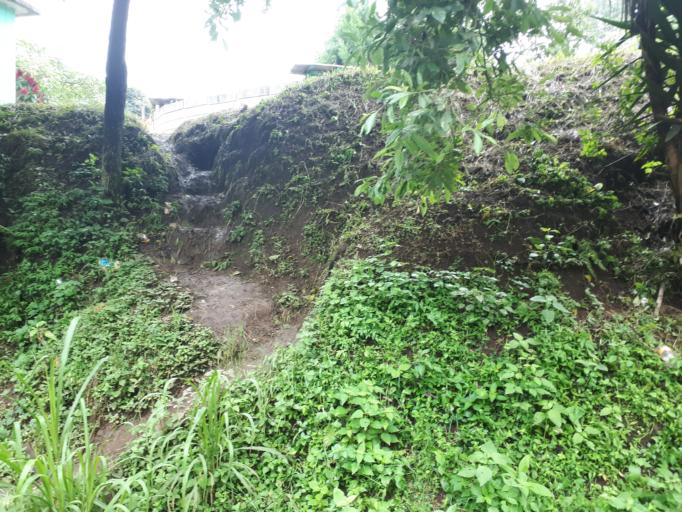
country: GT
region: Guatemala
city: Villa Canales
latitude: 14.4544
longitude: -90.5067
